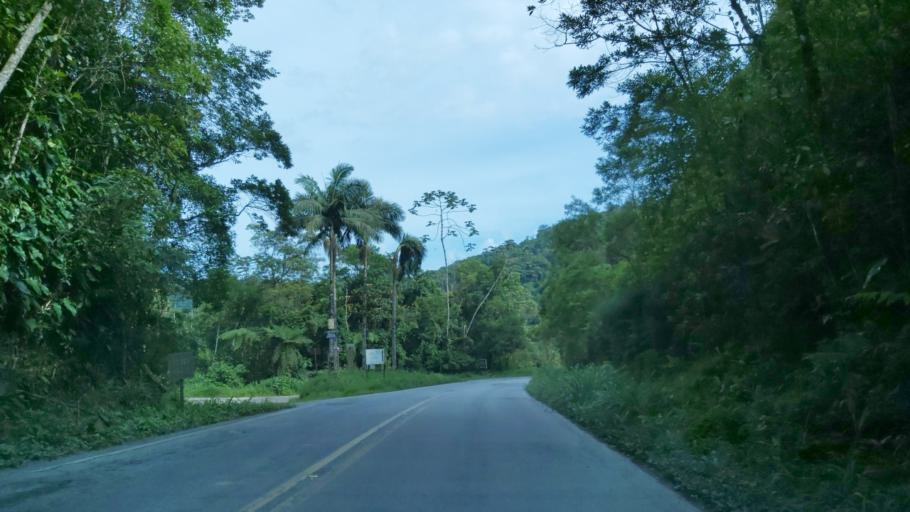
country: BR
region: Sao Paulo
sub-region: Pilar Do Sul
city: Pilar do Sul
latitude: -24.0309
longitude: -47.5583
